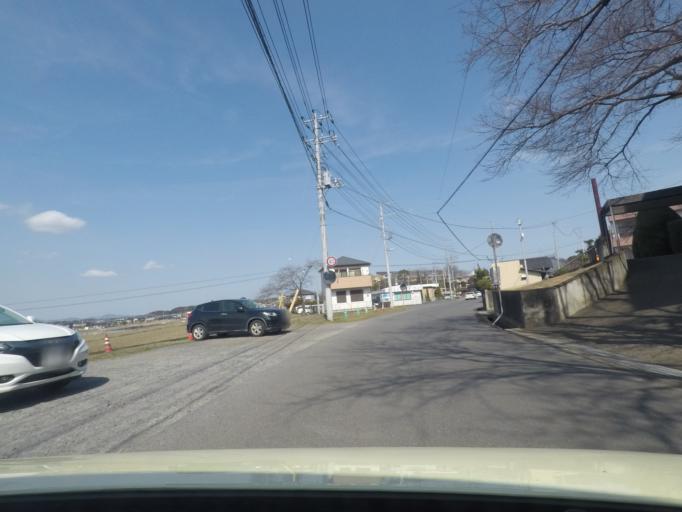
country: JP
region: Ibaraki
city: Ishioka
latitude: 36.1641
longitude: 140.3576
